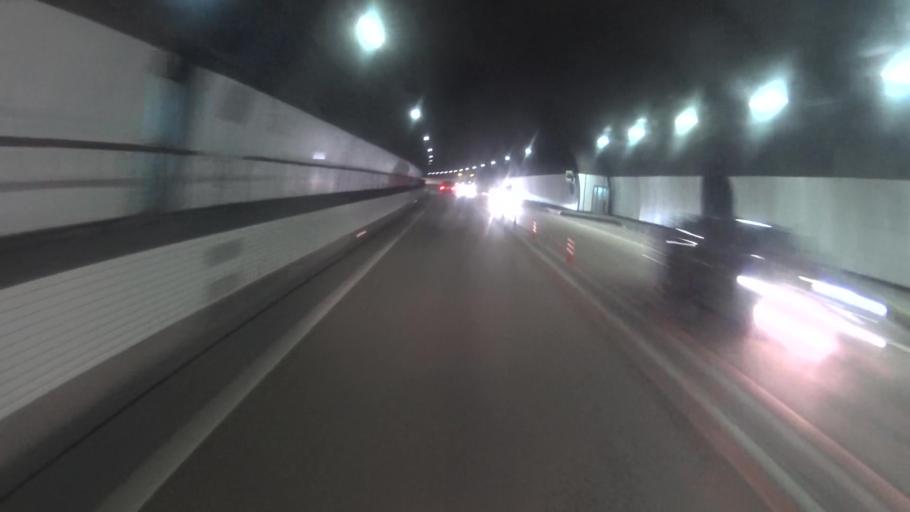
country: JP
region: Kyoto
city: Kameoka
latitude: 35.1395
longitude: 135.4472
